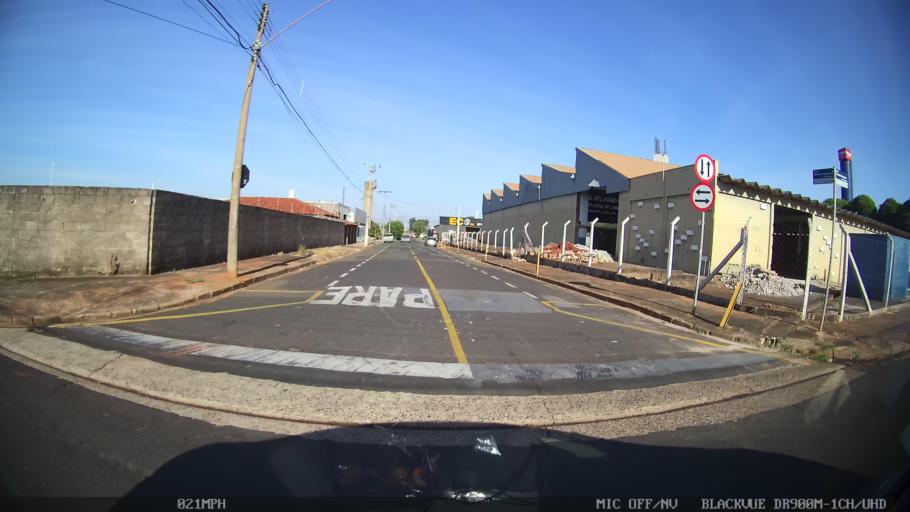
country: BR
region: Sao Paulo
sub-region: Sao Jose Do Rio Preto
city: Sao Jose do Rio Preto
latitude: -20.7870
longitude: -49.3565
